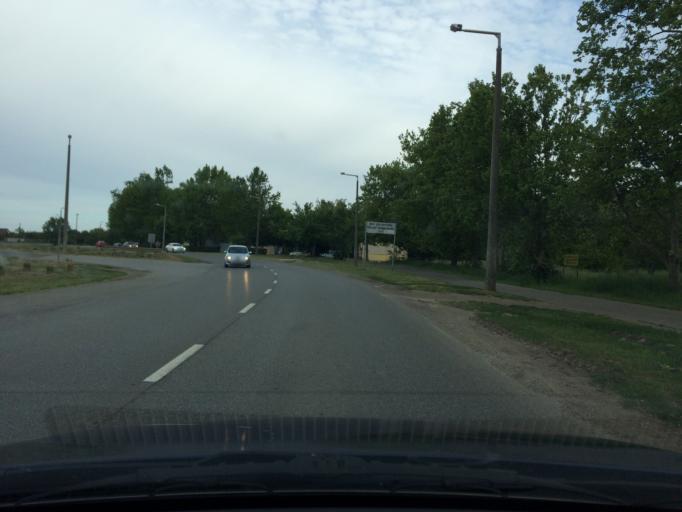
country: HU
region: Szabolcs-Szatmar-Bereg
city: Tiszavasvari
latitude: 47.9480
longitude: 21.3708
